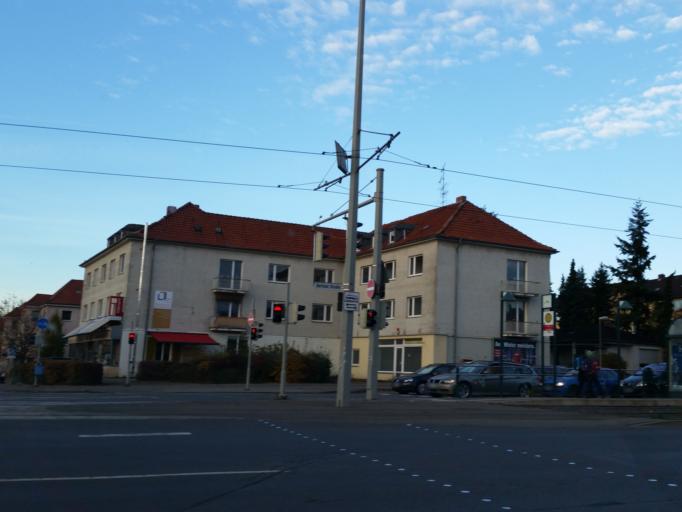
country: DE
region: Lower Saxony
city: Braunschweig
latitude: 52.2787
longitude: 10.5677
